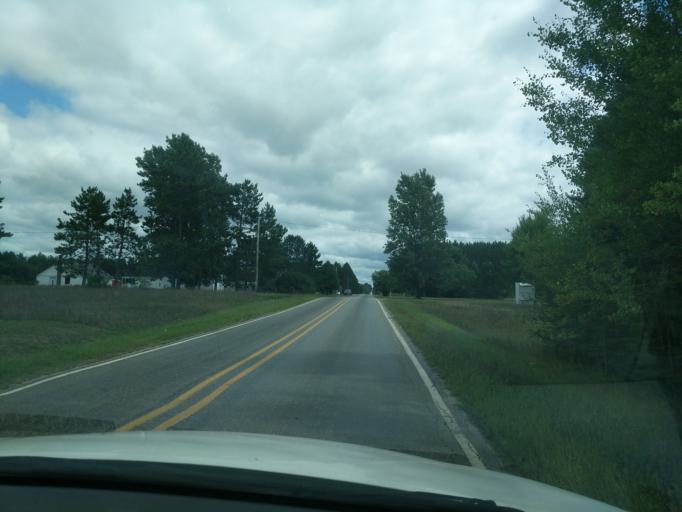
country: US
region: Michigan
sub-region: Wexford County
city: Manton
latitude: 44.3893
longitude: -85.4138
